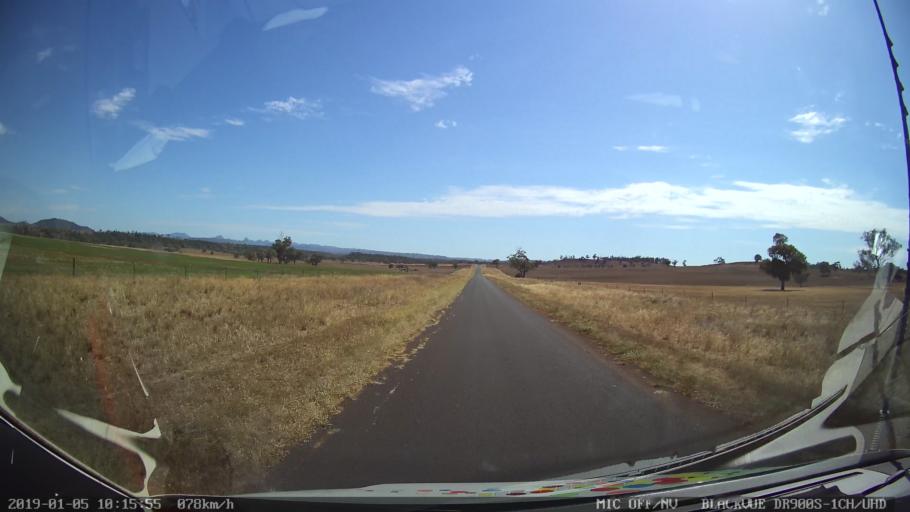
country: AU
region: New South Wales
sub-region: Gilgandra
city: Gilgandra
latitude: -31.5799
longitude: 148.9475
